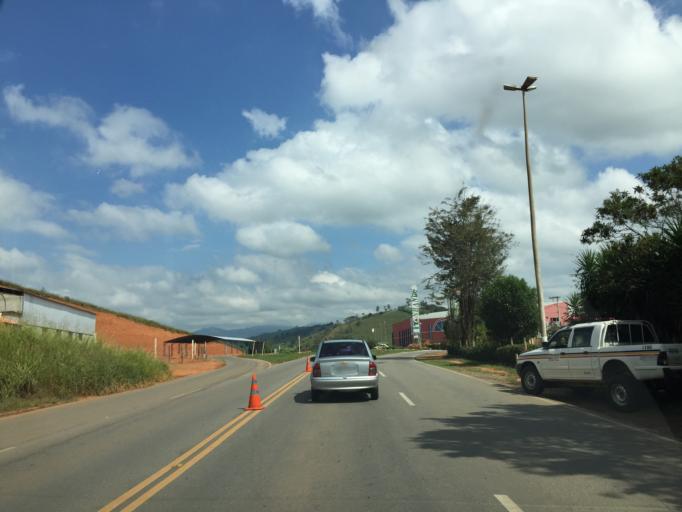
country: BR
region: Minas Gerais
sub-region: Itanhandu
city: Itanhandu
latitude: -22.3045
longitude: -44.9291
